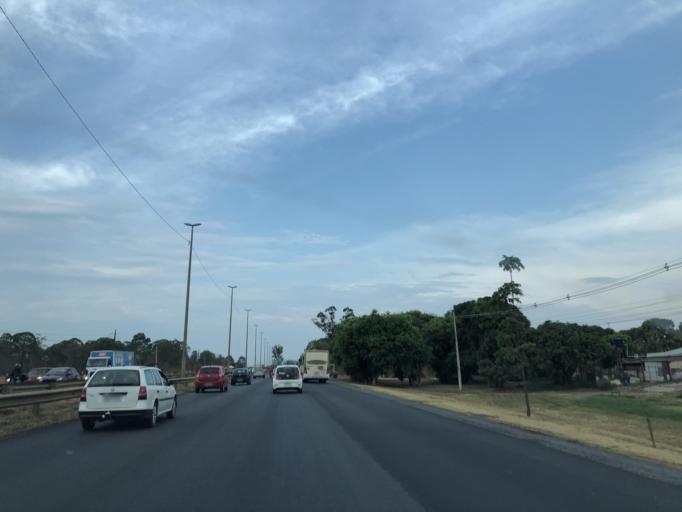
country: BR
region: Federal District
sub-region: Brasilia
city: Brasilia
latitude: -15.7951
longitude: -48.0624
